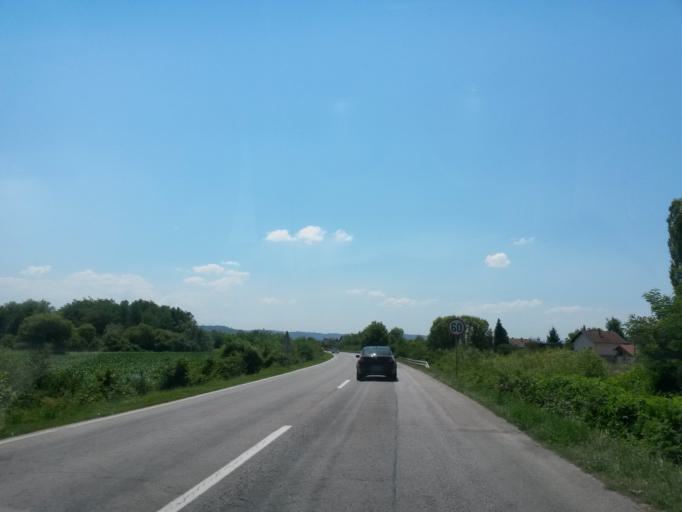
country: BA
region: Republika Srpska
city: Doboj
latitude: 44.8140
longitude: 18.0520
